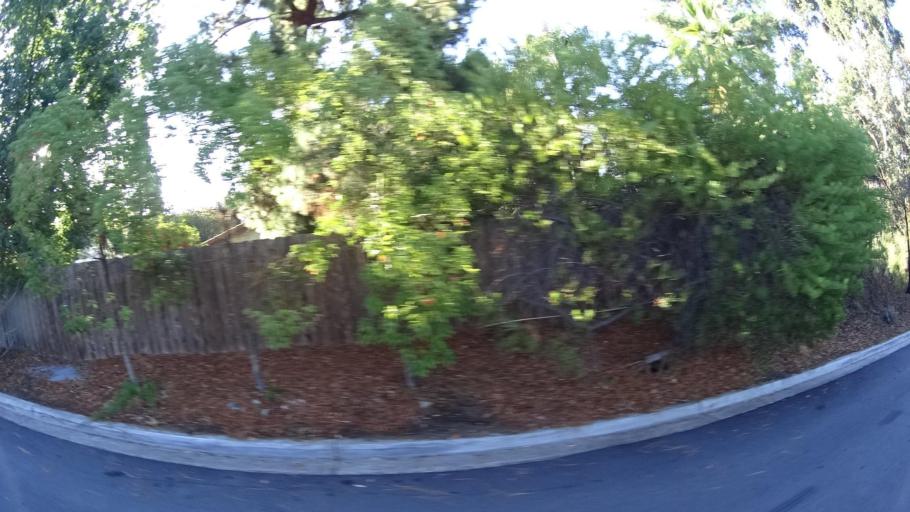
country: US
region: California
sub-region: San Diego County
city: Spring Valley
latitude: 32.7603
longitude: -116.9941
